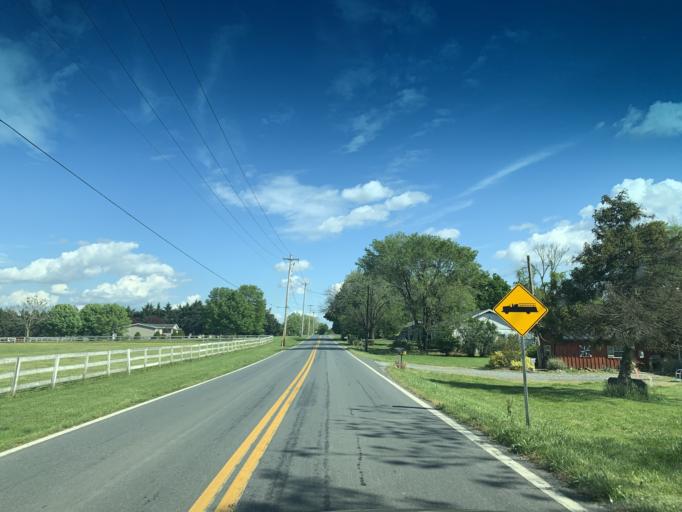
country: US
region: Maryland
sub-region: Cecil County
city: Rising Sun
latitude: 39.7095
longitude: -76.1485
